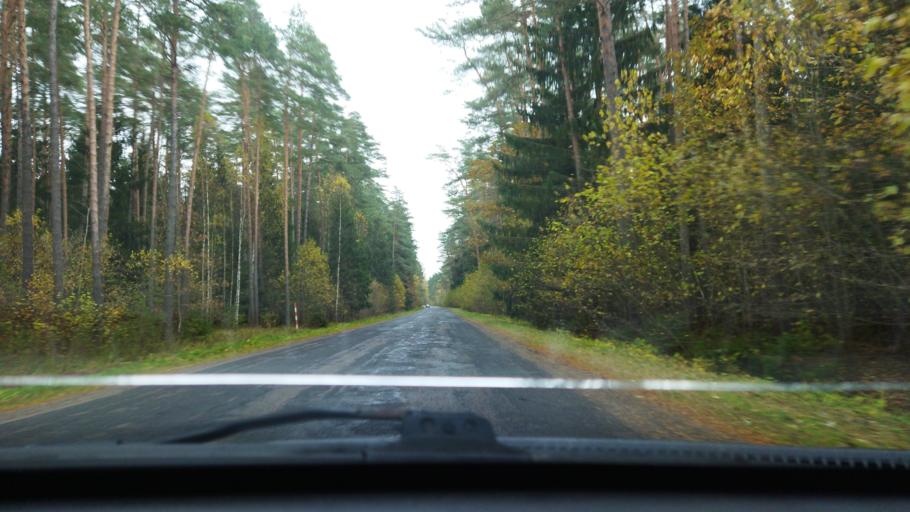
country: BY
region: Minsk
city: Svir
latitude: 54.8139
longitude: 26.1941
